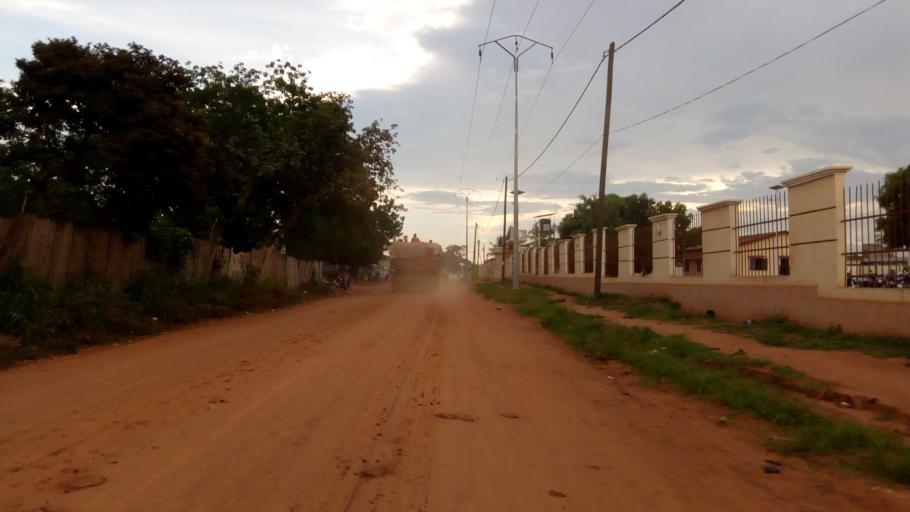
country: TG
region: Maritime
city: Lome
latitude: 6.2641
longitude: 1.1449
